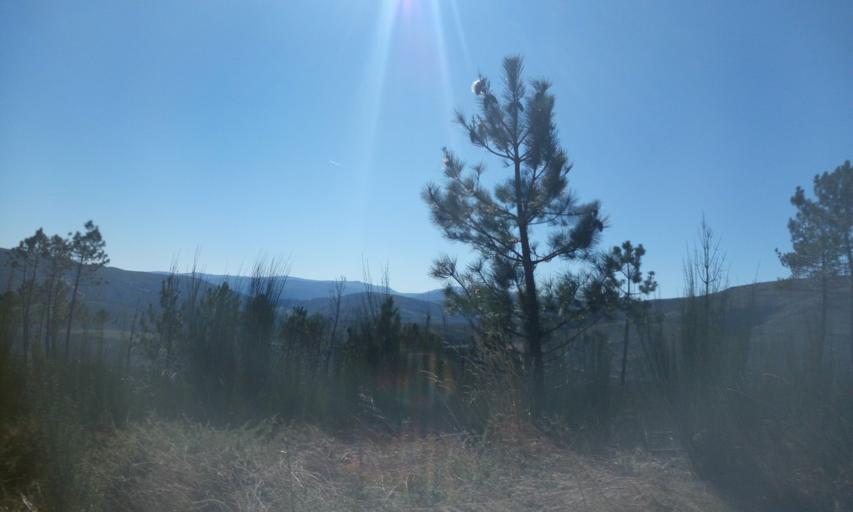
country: PT
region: Guarda
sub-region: Manteigas
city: Manteigas
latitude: 40.4749
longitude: -7.5081
